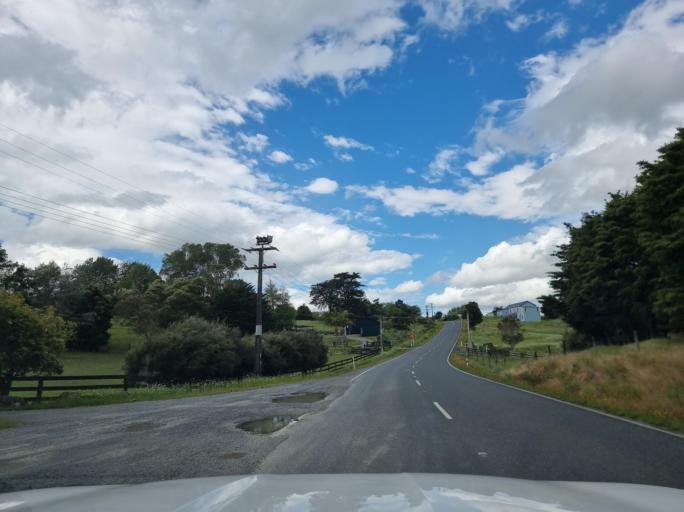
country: NZ
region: Northland
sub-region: Whangarei
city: Whangarei
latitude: -35.8461
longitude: 174.2851
